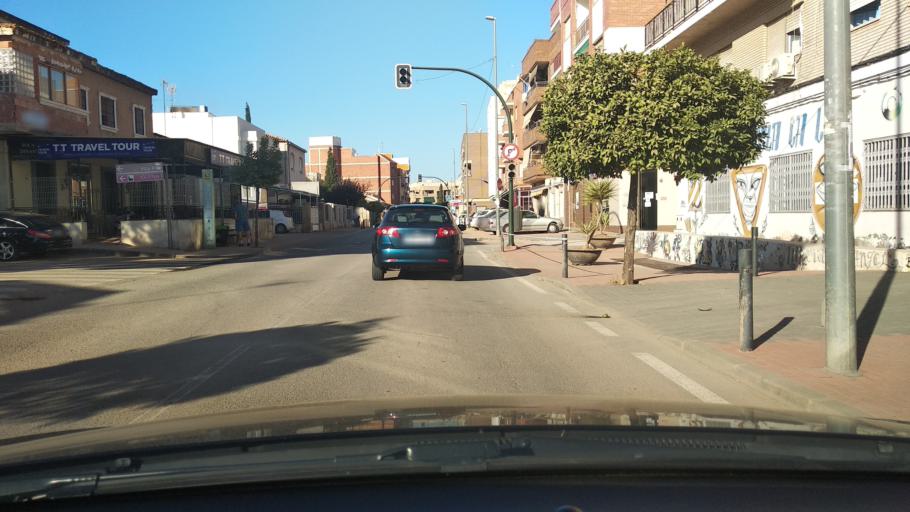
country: ES
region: Murcia
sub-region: Murcia
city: Murcia
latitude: 37.9442
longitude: -1.1275
